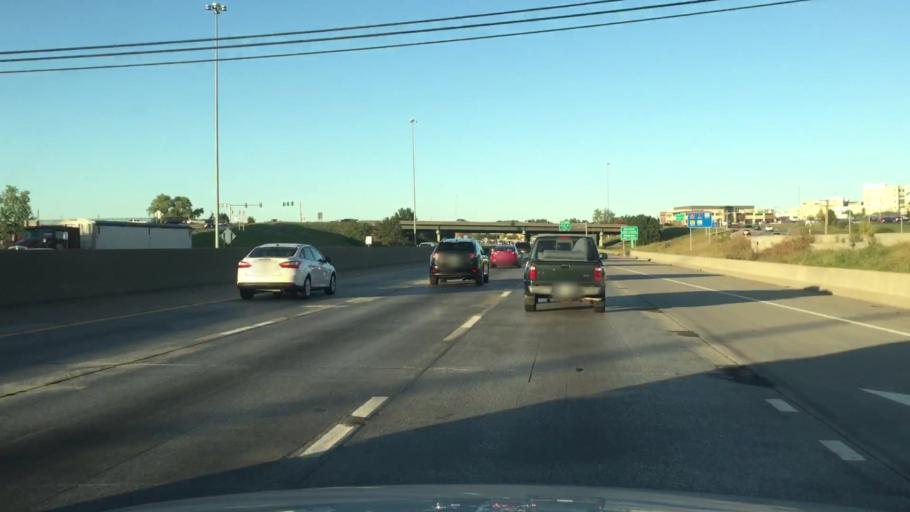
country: US
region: Kansas
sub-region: Johnson County
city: Overland Park
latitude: 38.9904
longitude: -94.7004
